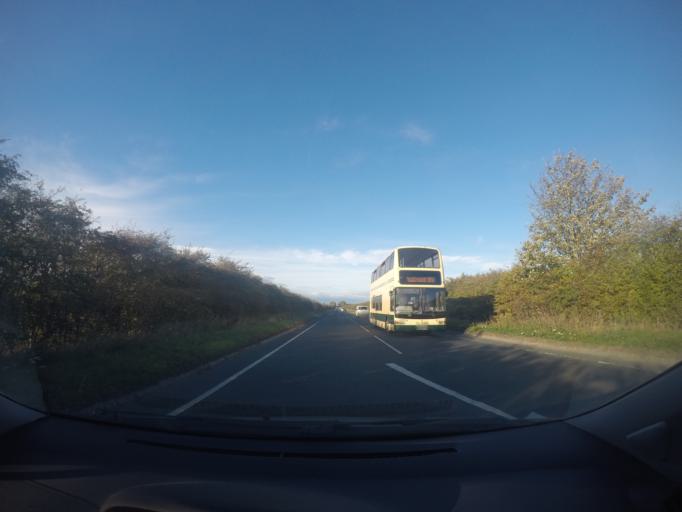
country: GB
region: England
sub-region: City of York
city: Copmanthorpe
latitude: 53.9400
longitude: -1.1453
